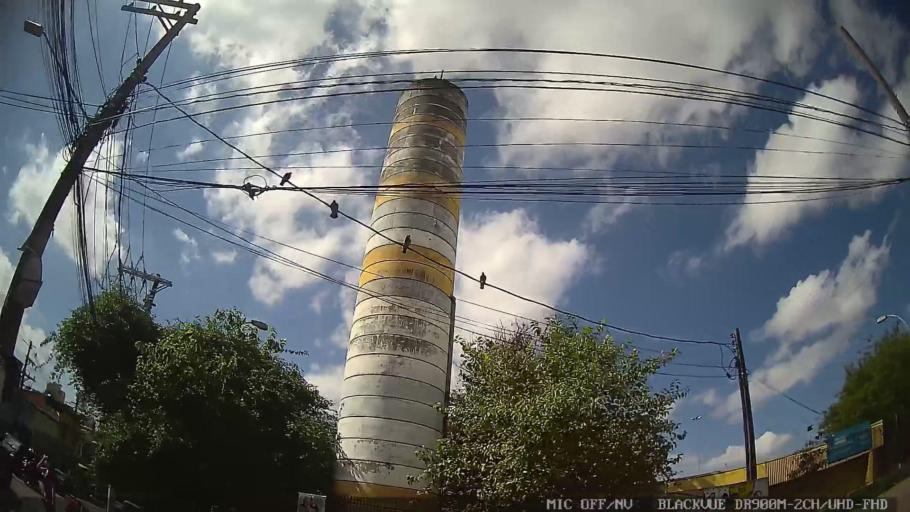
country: BR
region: Sao Paulo
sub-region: Sao Caetano Do Sul
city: Sao Caetano do Sul
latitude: -23.6235
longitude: -46.5910
